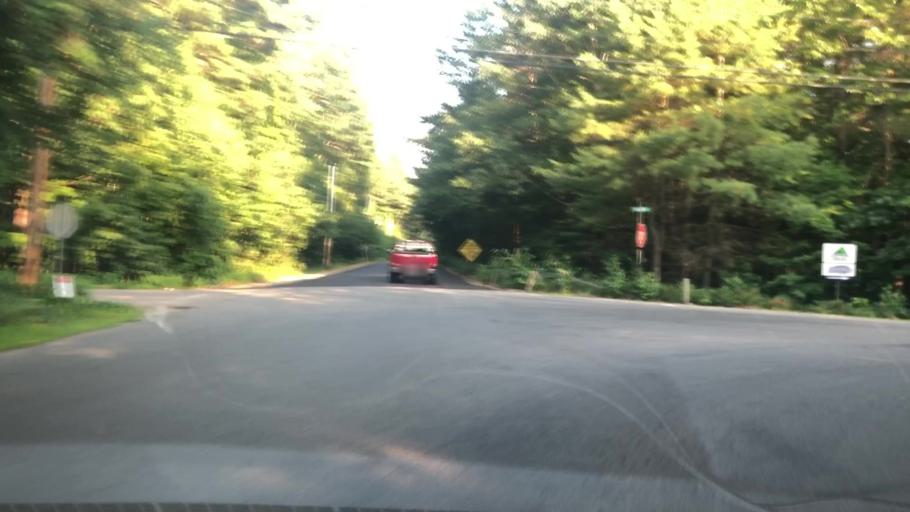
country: US
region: New Hampshire
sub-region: Hillsborough County
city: Milford
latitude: 42.8158
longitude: -71.6320
